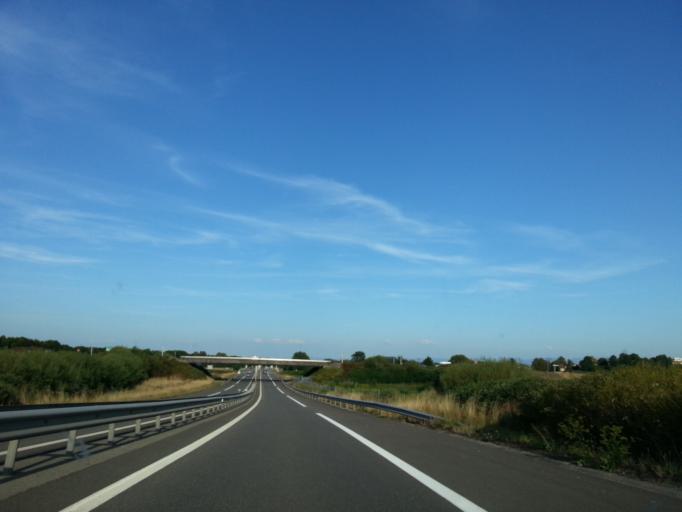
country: FR
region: Alsace
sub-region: Departement du Bas-Rhin
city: Haguenau
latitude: 48.8340
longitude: 7.7892
